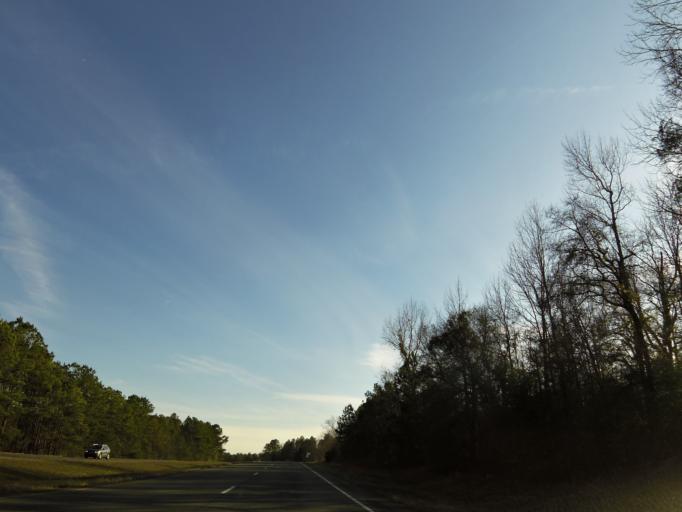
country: US
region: Georgia
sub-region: Stewart County
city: Richland
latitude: 32.1129
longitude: -84.6772
